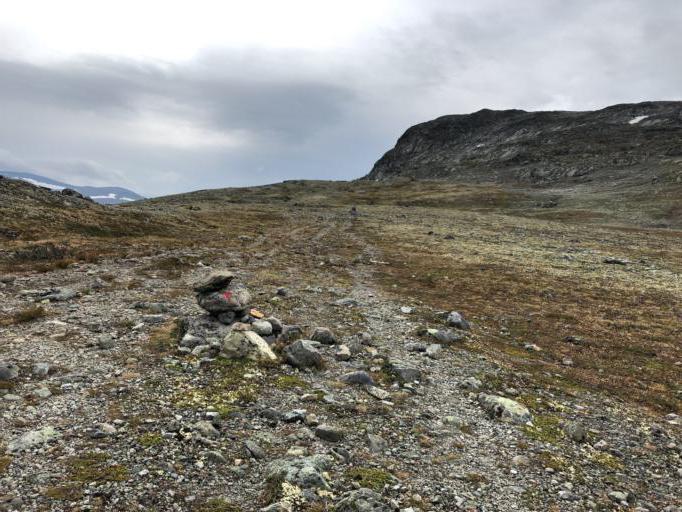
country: NO
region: Oppland
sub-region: Lom
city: Fossbergom
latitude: 61.5198
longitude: 8.8108
